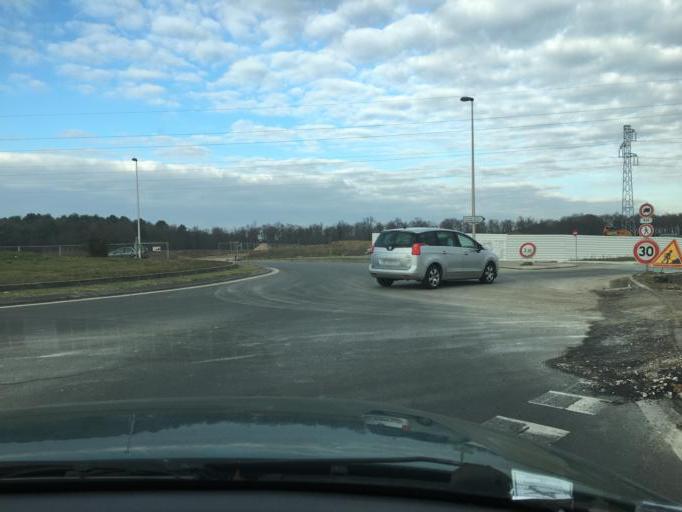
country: FR
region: Centre
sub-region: Departement du Loiret
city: Saran
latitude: 47.9602
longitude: 1.8808
